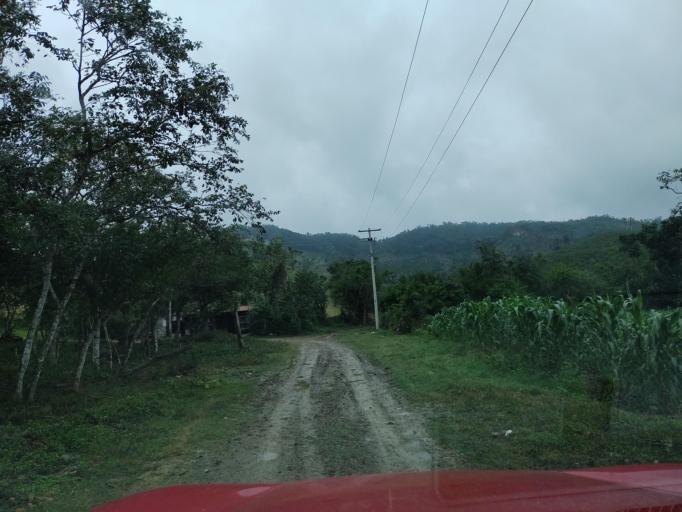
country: MX
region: Veracruz
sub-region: Papantla
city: El Chote
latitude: 20.3976
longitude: -97.3161
